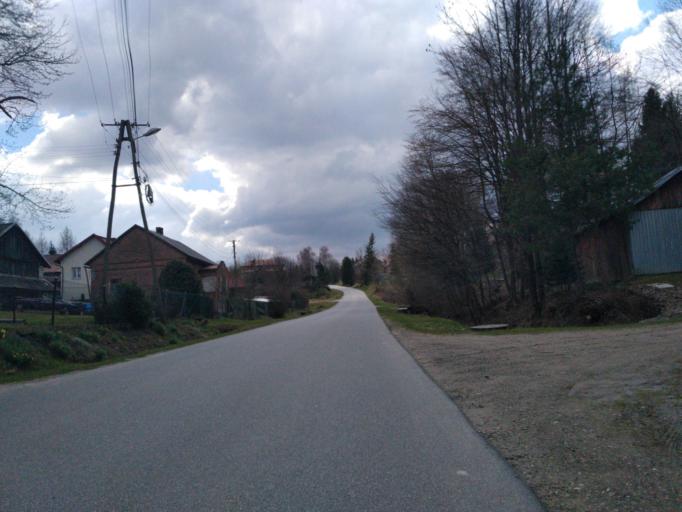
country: PL
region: Subcarpathian Voivodeship
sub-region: Powiat brzozowski
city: Dydnia
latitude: 49.6585
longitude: 22.2001
